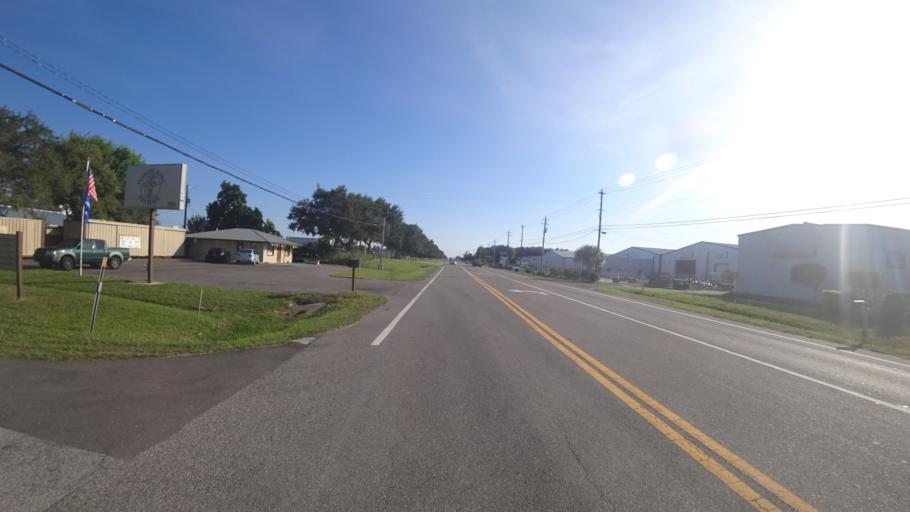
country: US
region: Florida
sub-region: Manatee County
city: Whitfield
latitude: 27.4149
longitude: -82.5467
